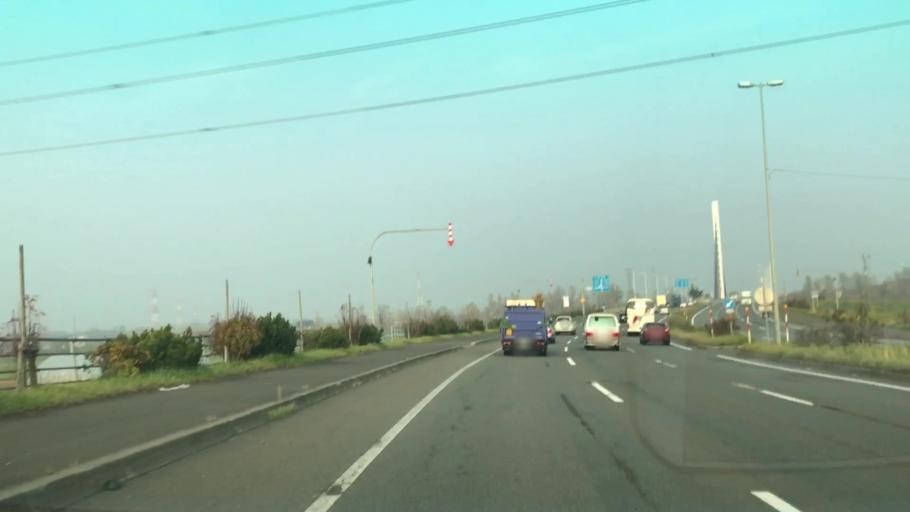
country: JP
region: Hokkaido
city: Ishikari
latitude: 43.1794
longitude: 141.3290
